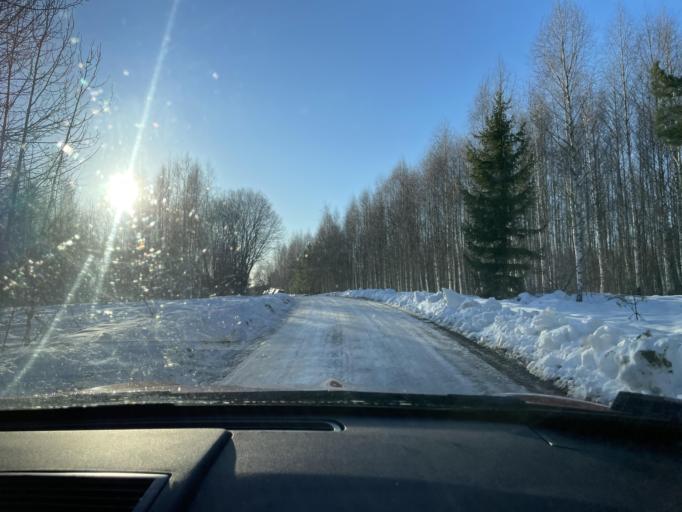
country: LV
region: Ludzas Rajons
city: Ludza
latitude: 56.4520
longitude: 27.6351
